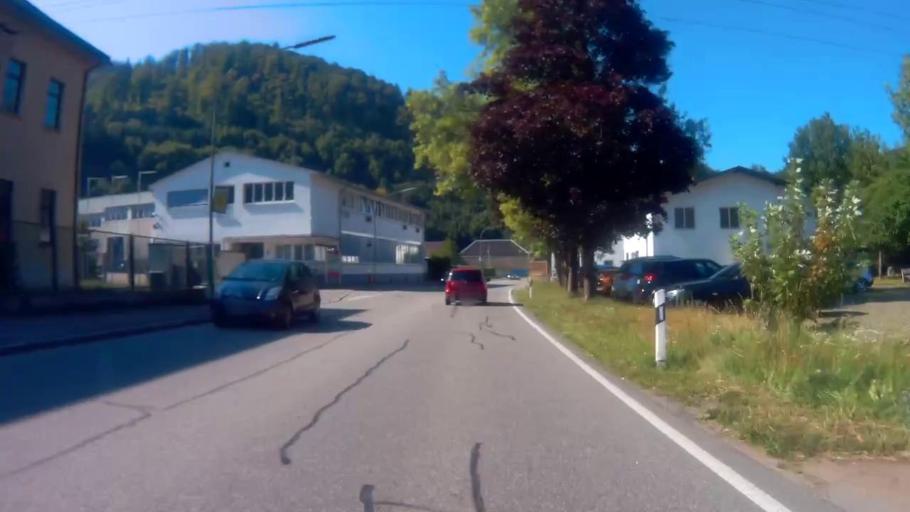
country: DE
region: Baden-Wuerttemberg
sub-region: Freiburg Region
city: Zell im Wiesental
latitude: 47.6992
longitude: 7.8459
